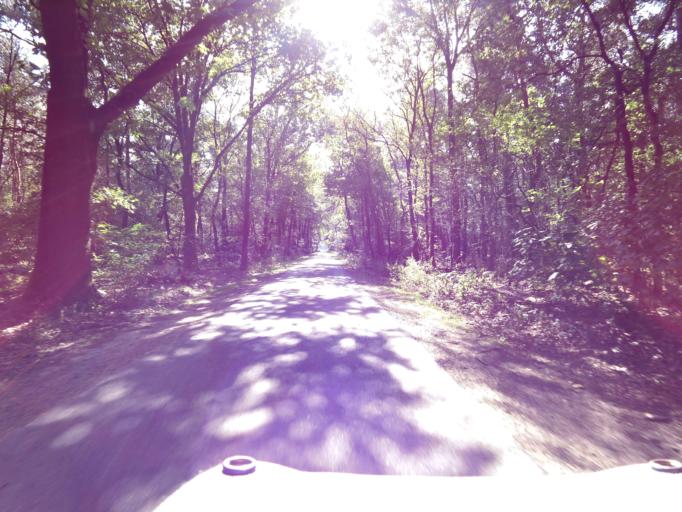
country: NL
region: Gelderland
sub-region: Gemeente Barneveld
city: Garderen
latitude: 52.2178
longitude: 5.7574
